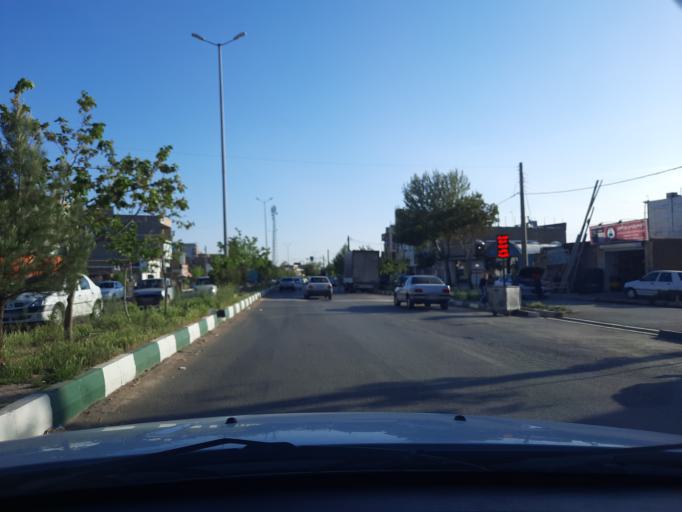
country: IR
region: Qazvin
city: Alvand
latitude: 36.2780
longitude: 50.1265
